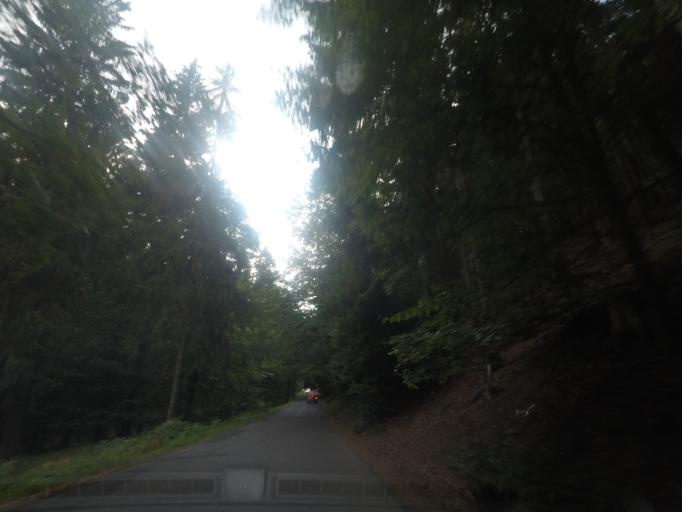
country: CZ
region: Ustecky
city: Mikulasovice
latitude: 50.8730
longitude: 14.3280
